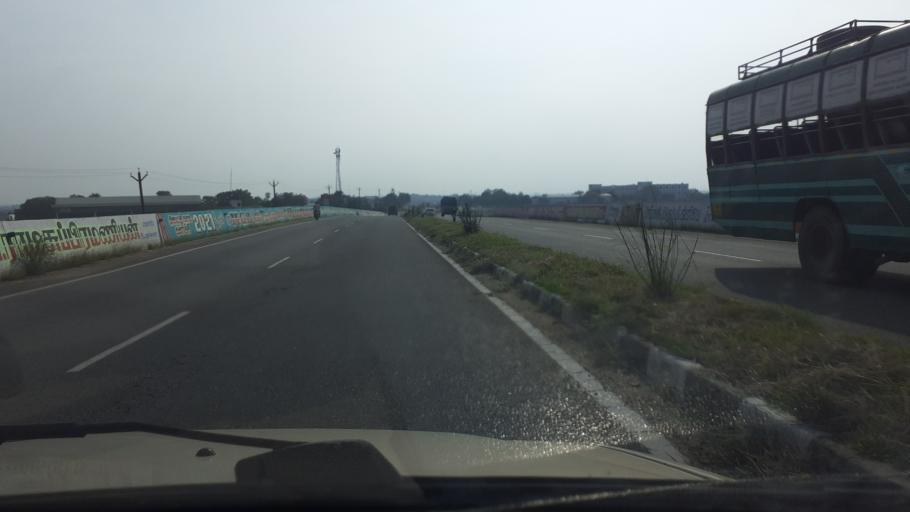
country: IN
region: Tamil Nadu
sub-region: Tirunelveli Kattabo
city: Tirunelveli
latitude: 8.6409
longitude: 77.7049
